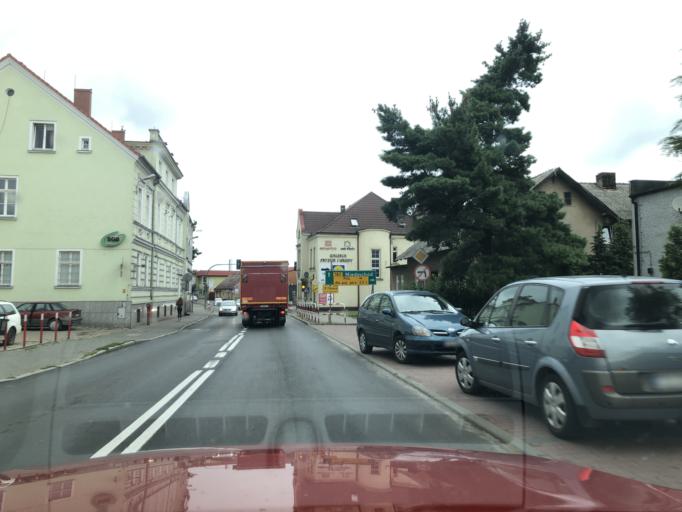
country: PL
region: Greater Poland Voivodeship
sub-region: Powiat szamotulski
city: Wronki
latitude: 52.7072
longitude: 16.3797
